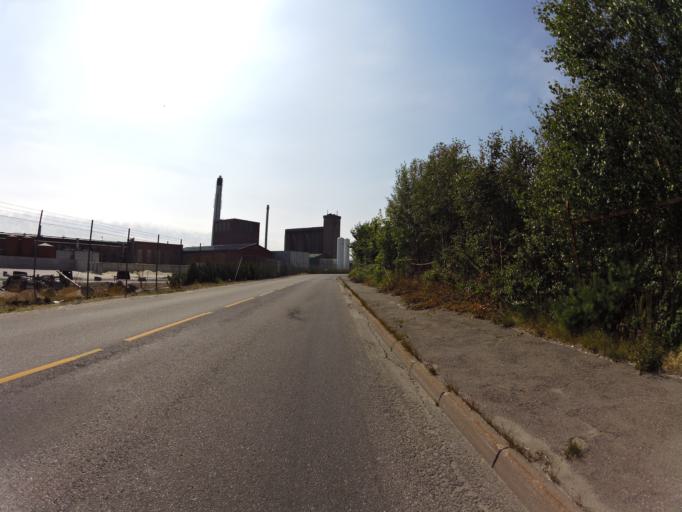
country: NO
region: Ostfold
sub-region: Sarpsborg
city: Sarpsborg
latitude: 59.2646
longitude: 11.0385
